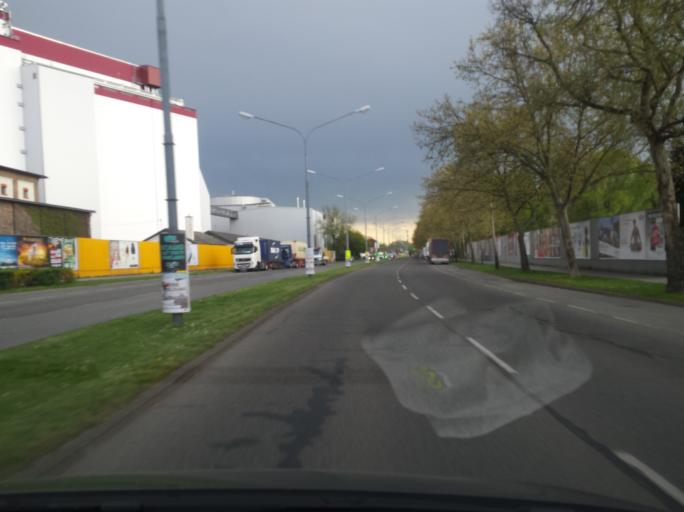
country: AT
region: Lower Austria
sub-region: Politischer Bezirk Wien-Umgebung
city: Gerasdorf bei Wien
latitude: 48.2256
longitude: 16.4448
